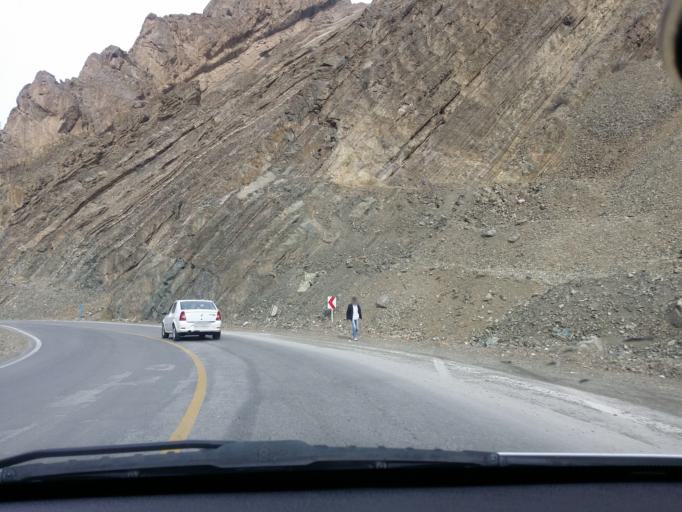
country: IR
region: Tehran
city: Tajrish
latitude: 36.0208
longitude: 51.2673
